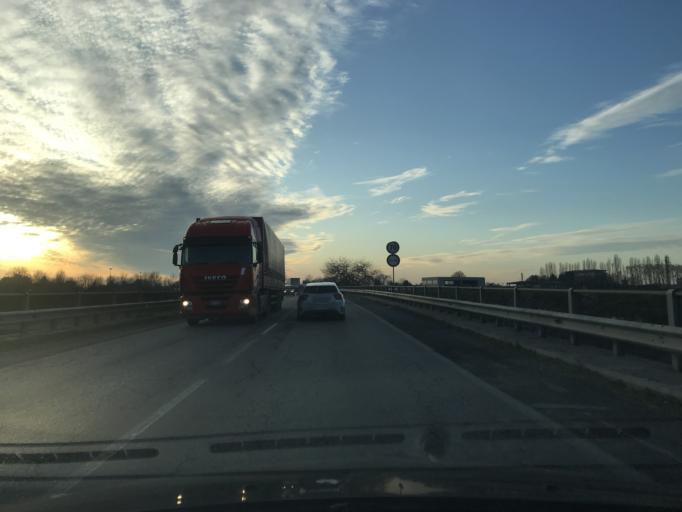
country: IT
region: Lombardy
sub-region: Provincia di Lodi
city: Castiraga Vidardo
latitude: 45.2487
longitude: 9.4100
